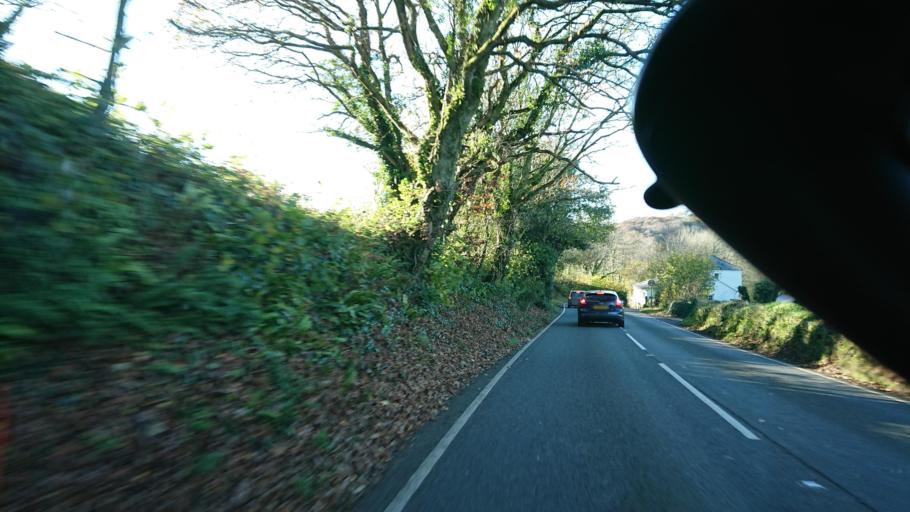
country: GB
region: England
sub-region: Cornwall
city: Looe
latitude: 50.3919
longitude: -4.3776
